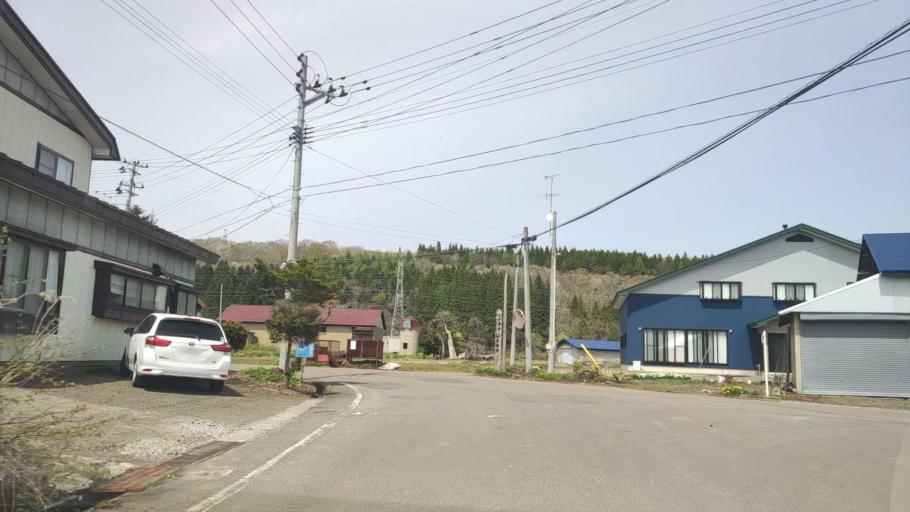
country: JP
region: Aomori
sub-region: Misawa Shi
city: Inuotose
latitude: 40.7890
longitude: 141.1094
